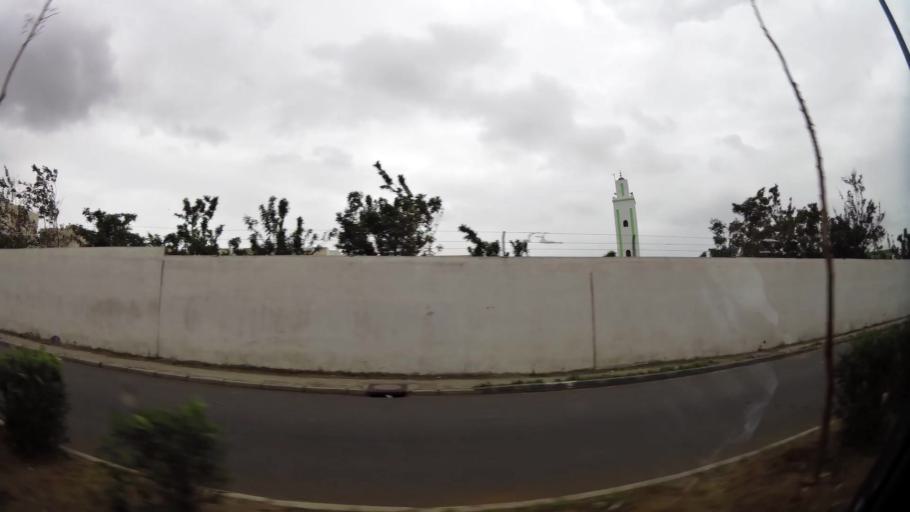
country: MA
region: Grand Casablanca
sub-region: Casablanca
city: Casablanca
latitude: 33.5702
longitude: -7.5636
